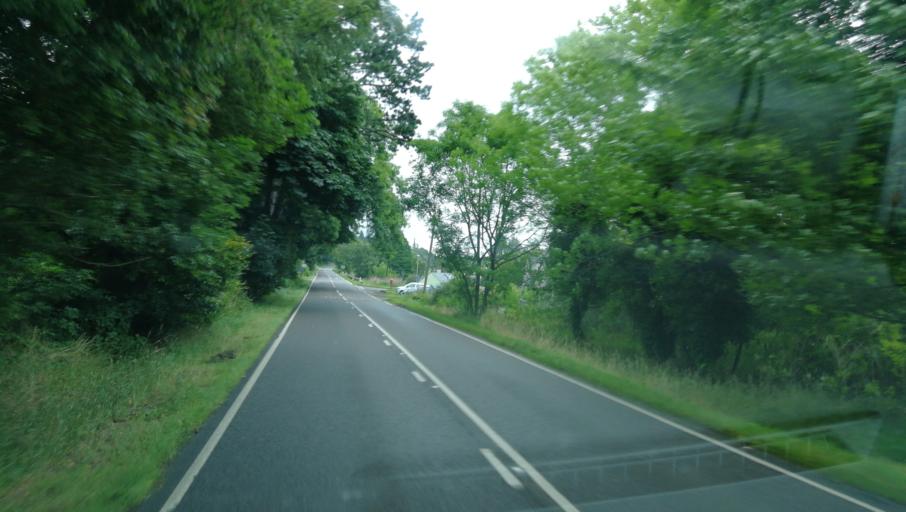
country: GB
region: Scotland
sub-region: Highland
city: Inverness
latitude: 57.4082
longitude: -4.3394
